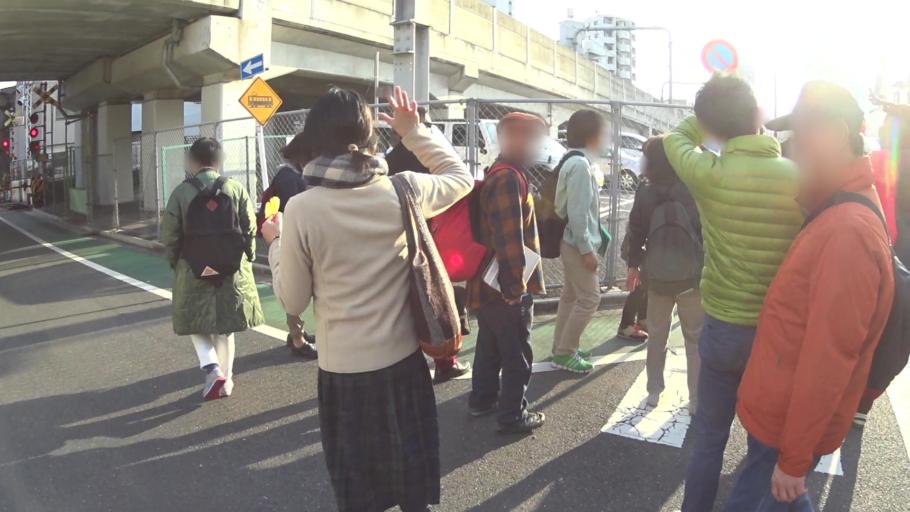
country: JP
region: Tokyo
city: Urayasu
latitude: 35.7131
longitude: 139.8157
